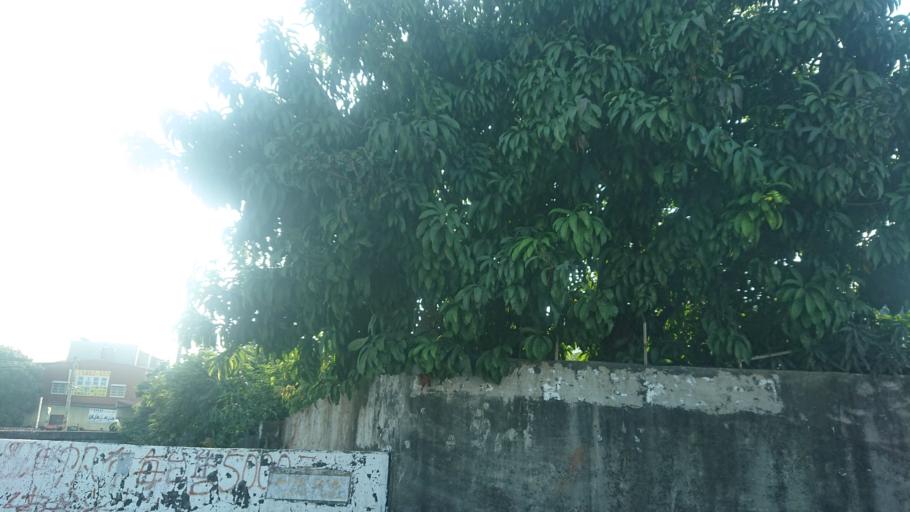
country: TW
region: Taiwan
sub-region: Tainan
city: Tainan
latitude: 23.0740
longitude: 120.2138
